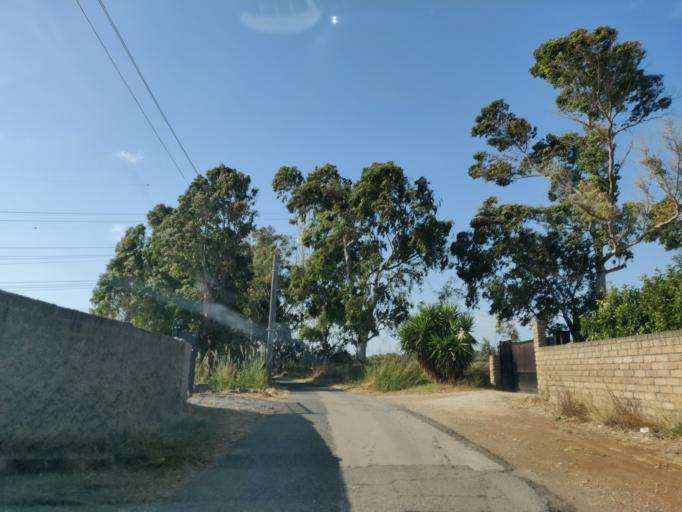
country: IT
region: Latium
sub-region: Citta metropolitana di Roma Capitale
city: Aurelia
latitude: 42.1305
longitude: 11.7665
